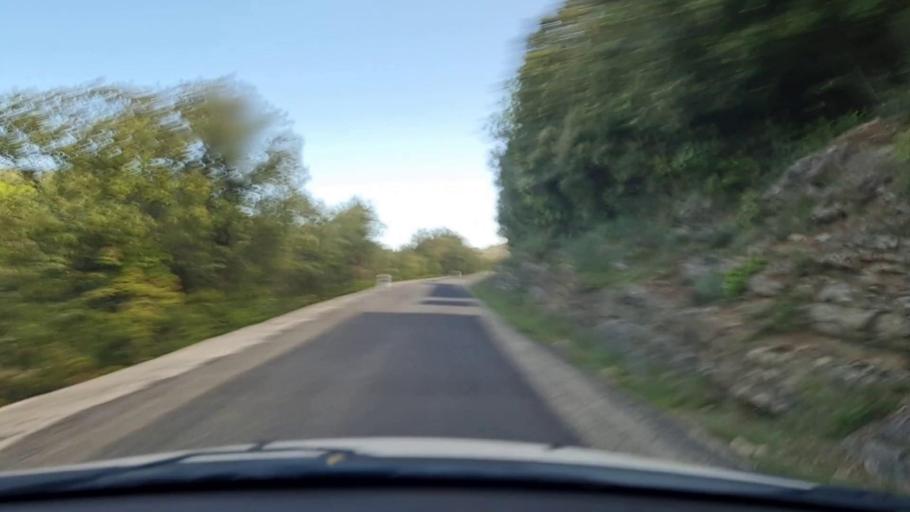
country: FR
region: Languedoc-Roussillon
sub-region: Departement du Gard
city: Les Salles-du-Gardon
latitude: 44.1790
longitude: 4.0205
